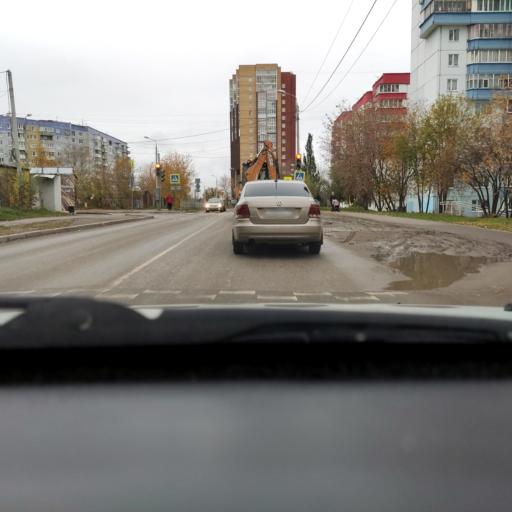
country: RU
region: Perm
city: Perm
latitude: 58.0322
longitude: 56.3258
